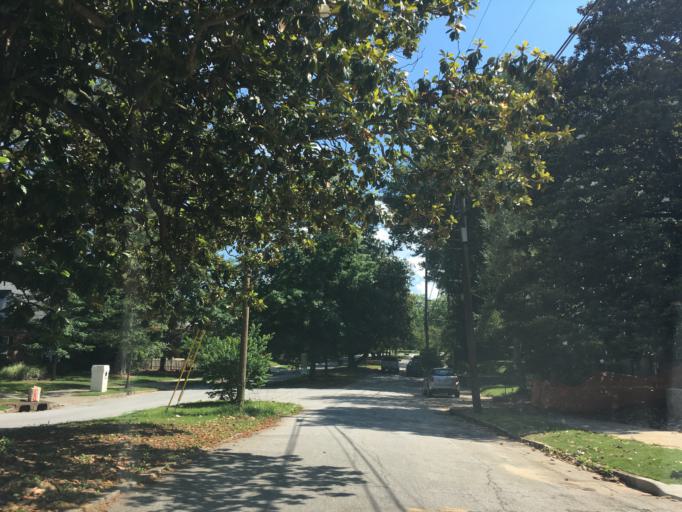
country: US
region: Georgia
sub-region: DeKalb County
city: Druid Hills
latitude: 33.7864
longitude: -84.3500
